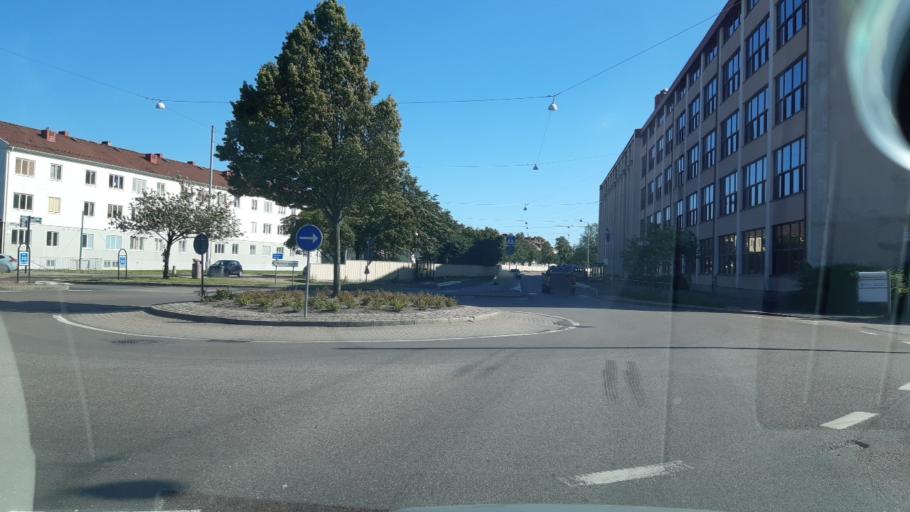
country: SE
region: Vaestra Goetaland
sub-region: Goteborg
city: Goeteborg
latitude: 57.7331
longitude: 12.0070
